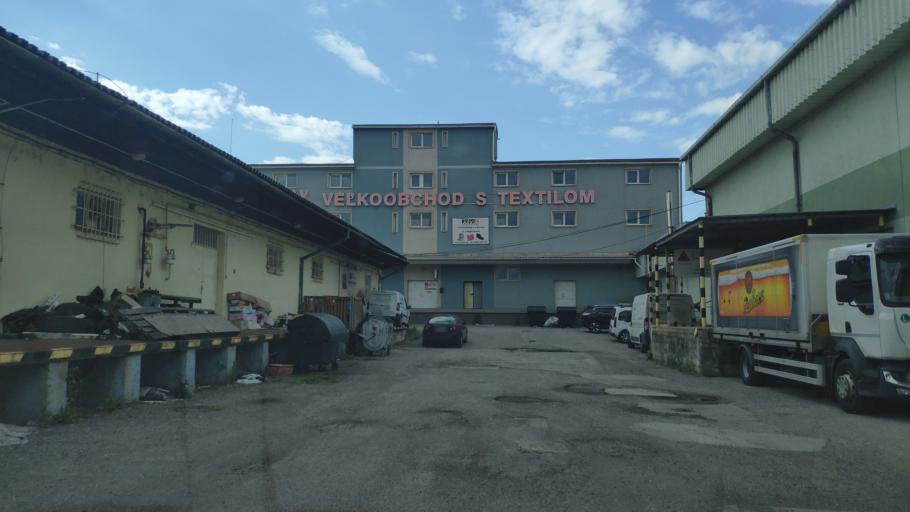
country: SK
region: Kosicky
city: Kosice
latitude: 48.7009
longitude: 21.2645
